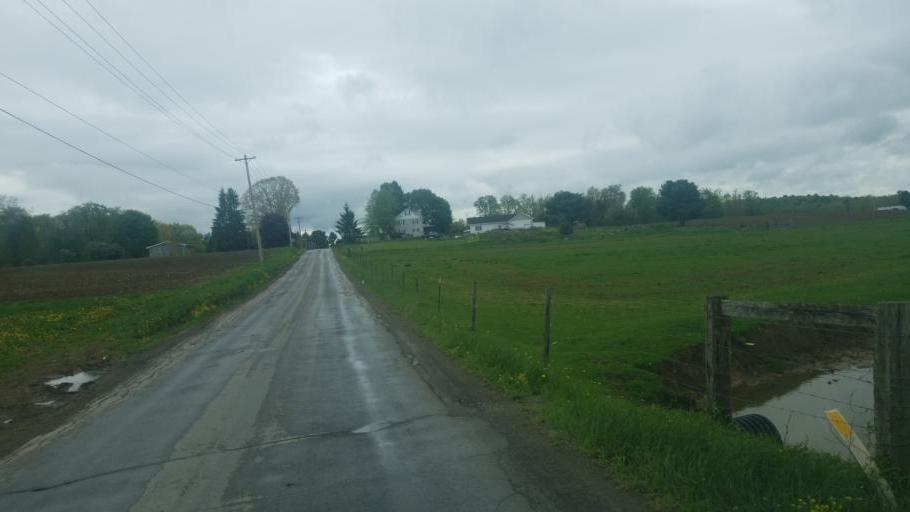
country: US
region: Pennsylvania
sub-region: Forest County
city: Tionesta
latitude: 41.4018
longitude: -79.3880
